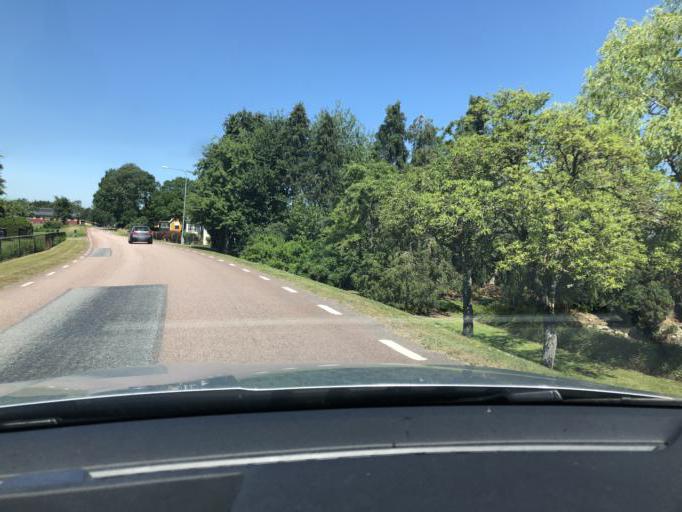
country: SE
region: Blekinge
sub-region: Olofstroms Kommun
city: Jamshog
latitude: 56.1797
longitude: 14.6126
